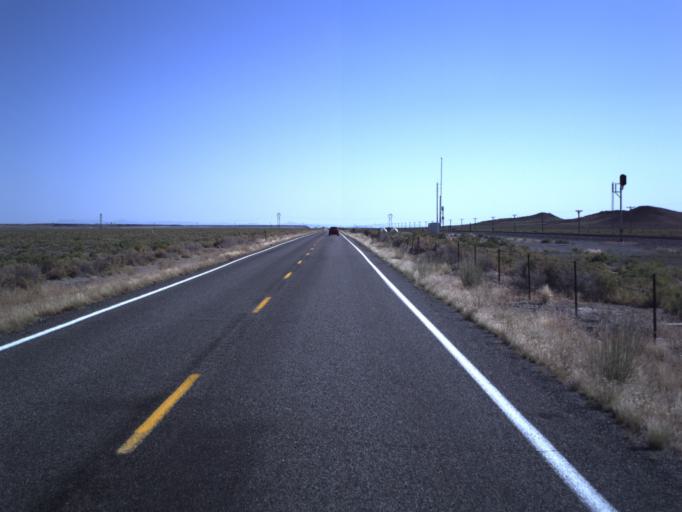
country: US
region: Utah
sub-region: Millard County
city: Delta
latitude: 39.1404
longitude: -112.7252
